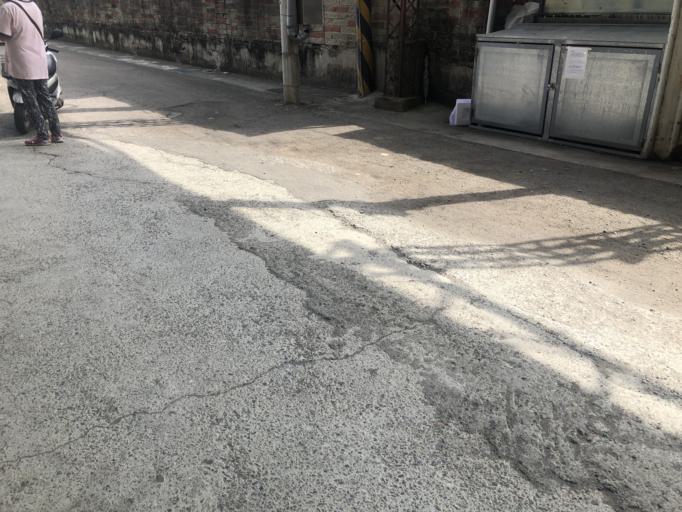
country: TW
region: Taiwan
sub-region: Changhua
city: Chang-hua
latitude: 24.1374
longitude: 120.6019
